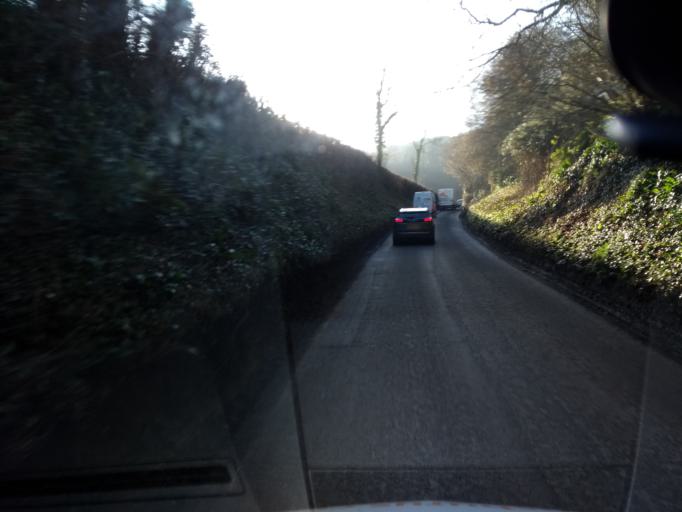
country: GB
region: England
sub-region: Somerset
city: Bruton
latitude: 51.1313
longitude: -2.4756
